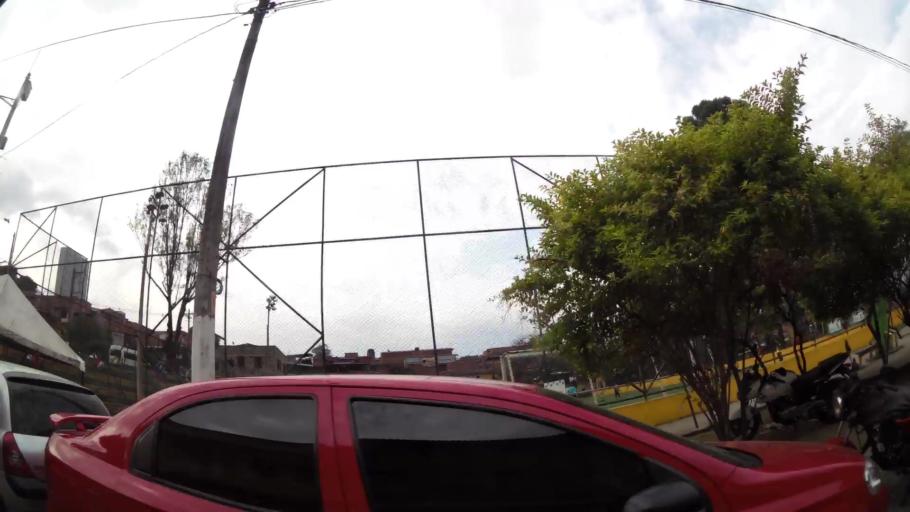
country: CO
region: Antioquia
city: Medellin
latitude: 6.2892
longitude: -75.5556
